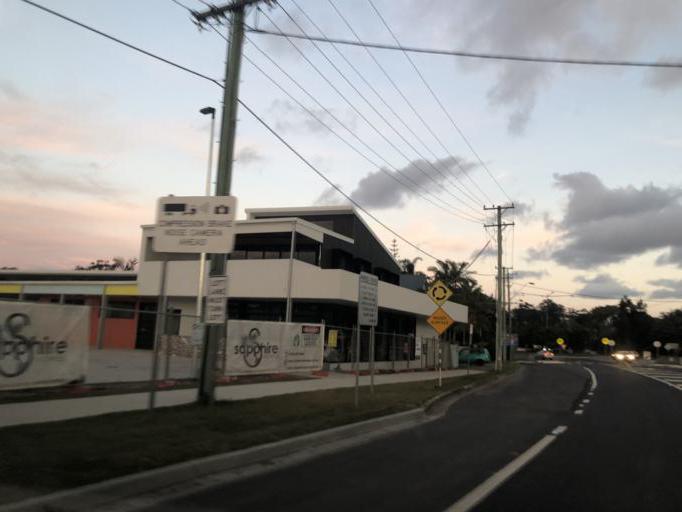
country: AU
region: New South Wales
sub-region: Coffs Harbour
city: Woolgoolga
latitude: -30.1118
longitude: 153.1903
